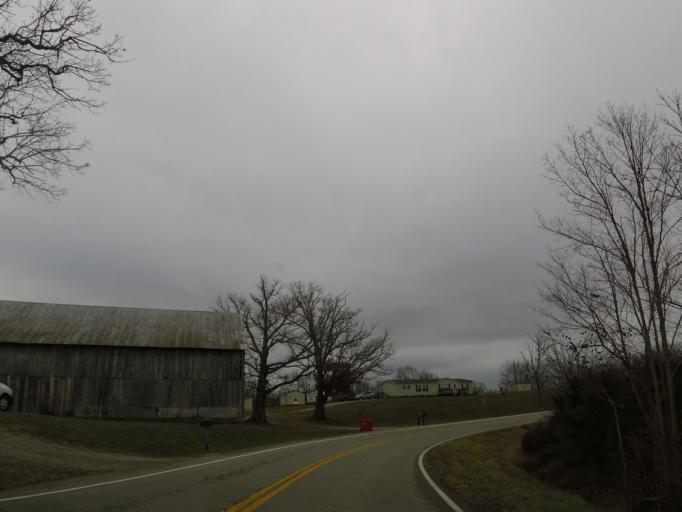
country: US
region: Kentucky
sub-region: Franklin County
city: Frankfort
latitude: 38.3434
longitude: -84.9646
